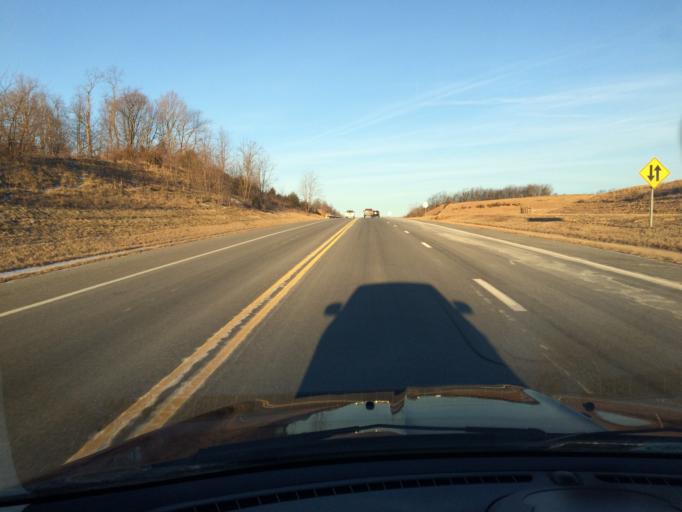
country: US
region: Virginia
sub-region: City of Staunton
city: Staunton
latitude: 38.1350
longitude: -79.0977
